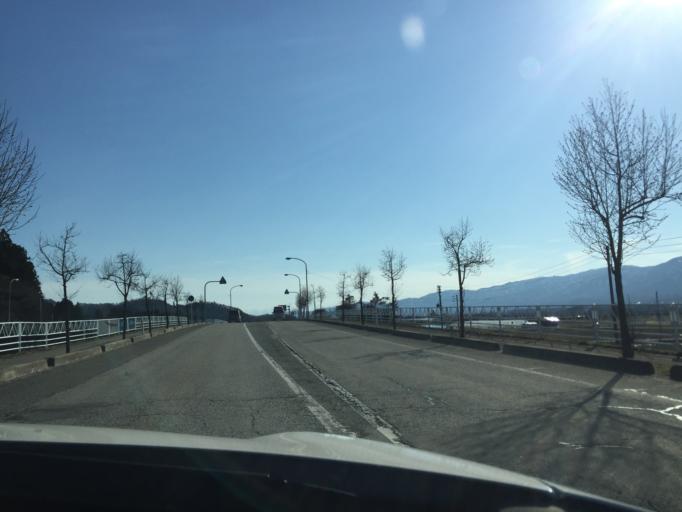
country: JP
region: Yamagata
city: Nagai
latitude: 38.1722
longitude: 140.0910
